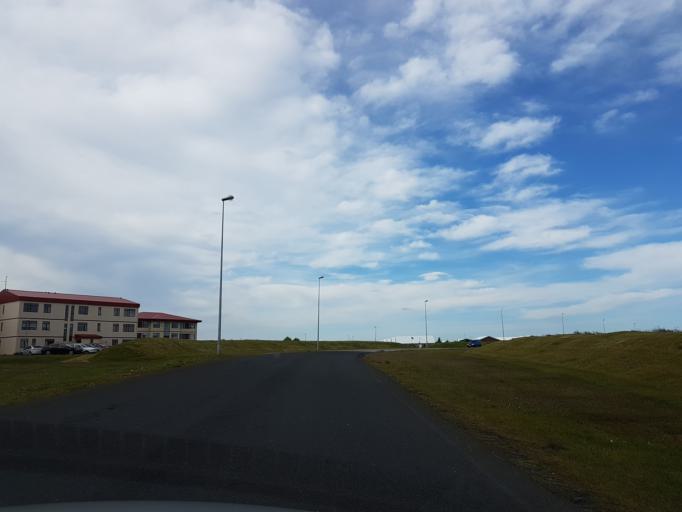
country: IS
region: Southern Peninsula
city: Reykjanesbaer
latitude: 64.0108
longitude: -22.5789
